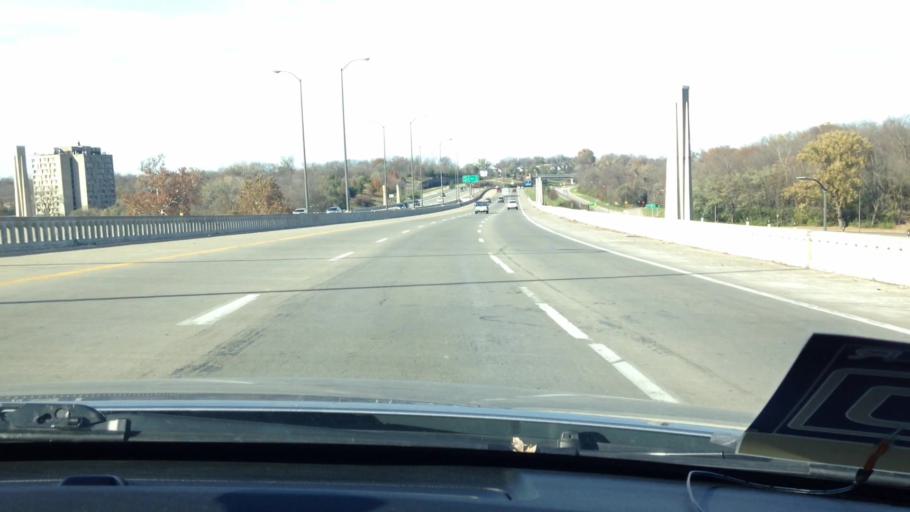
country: US
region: Kansas
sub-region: Johnson County
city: Westwood
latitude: 39.0399
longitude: -94.5596
